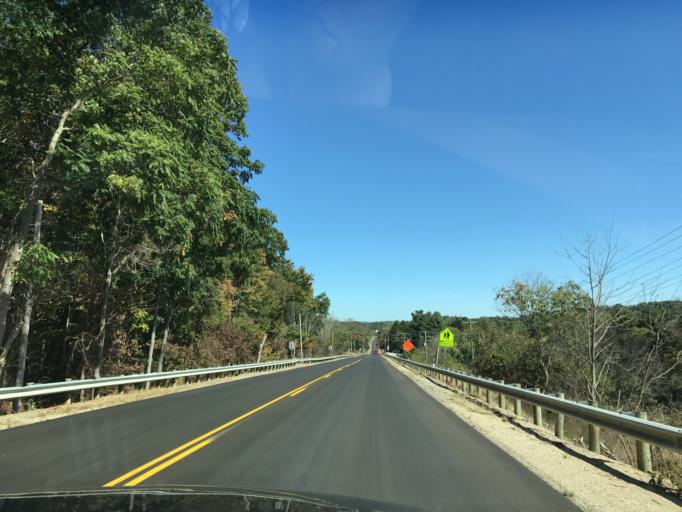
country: US
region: Ohio
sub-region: Muskingum County
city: Pleasant Grove
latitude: 39.9697
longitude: -81.8633
